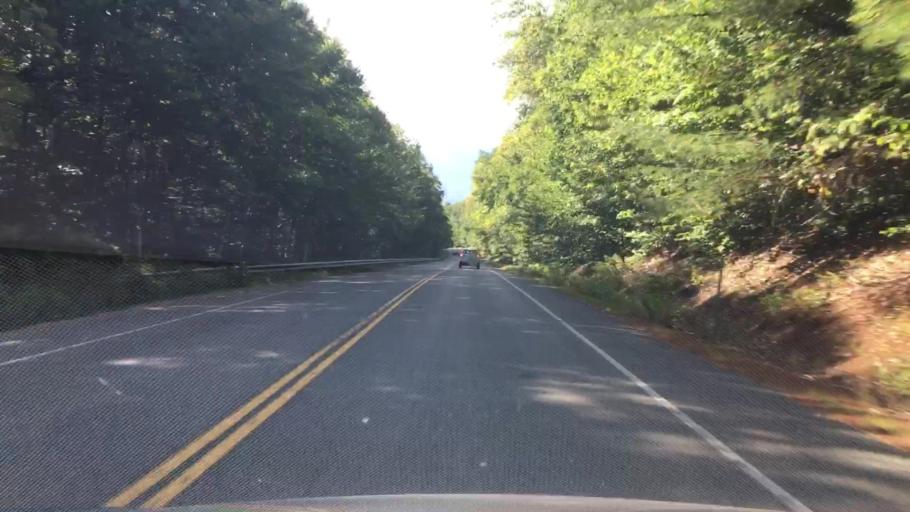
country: US
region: New Hampshire
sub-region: Grafton County
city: Woodstock
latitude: 44.0514
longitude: -71.5691
